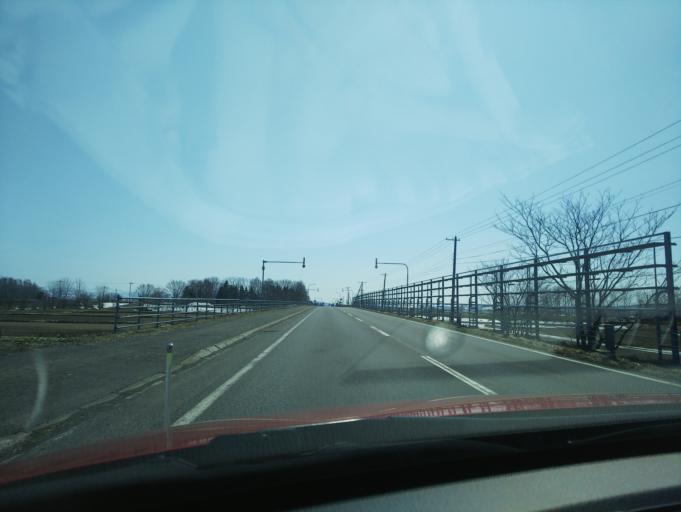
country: JP
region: Hokkaido
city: Nayoro
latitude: 44.2234
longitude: 142.3949
